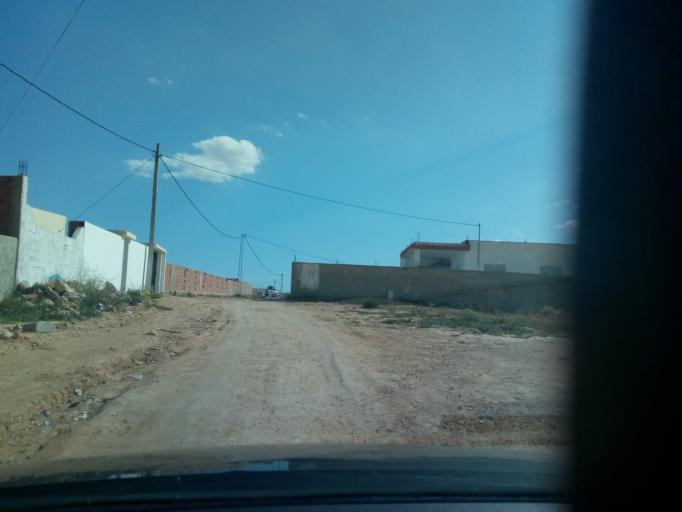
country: TN
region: Safaqis
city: Sfax
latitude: 34.7300
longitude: 10.6047
